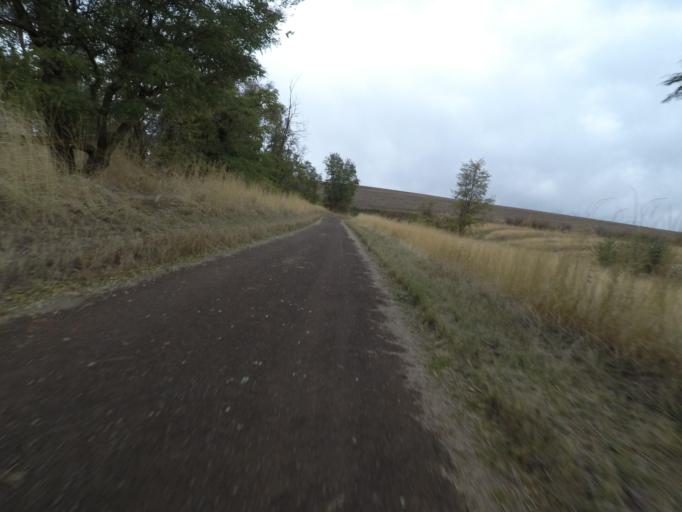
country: US
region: Washington
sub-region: Walla Walla County
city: Walla Walla East
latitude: 46.0606
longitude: -118.2569
